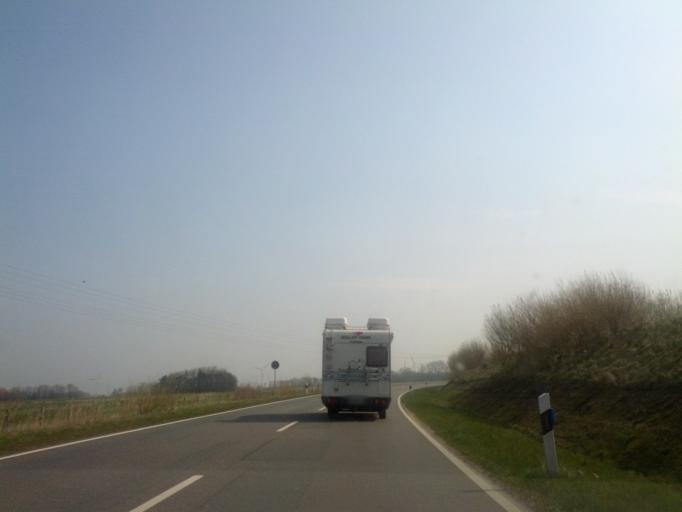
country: DE
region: Lower Saxony
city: Norden
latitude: 53.6150
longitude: 7.1889
